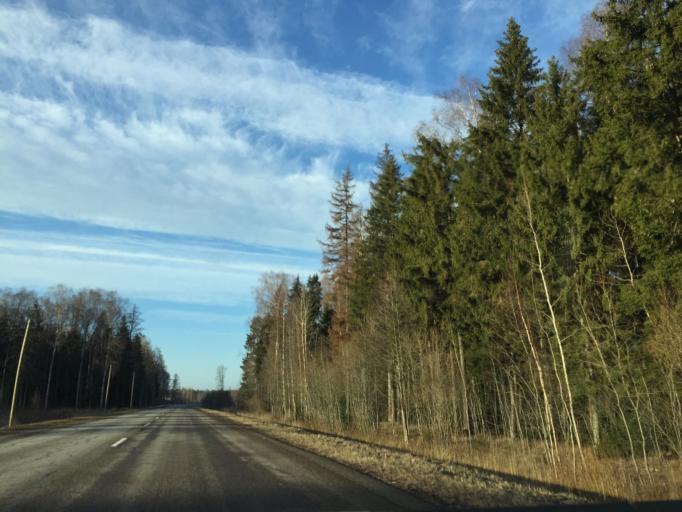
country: LV
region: Kekava
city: Balozi
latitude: 56.8083
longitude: 24.0677
